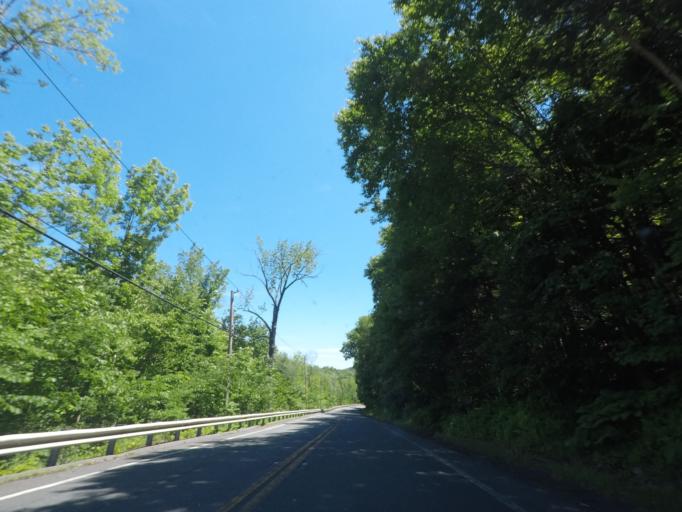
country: US
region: Massachusetts
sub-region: Berkshire County
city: Becket
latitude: 42.2623
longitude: -72.9618
